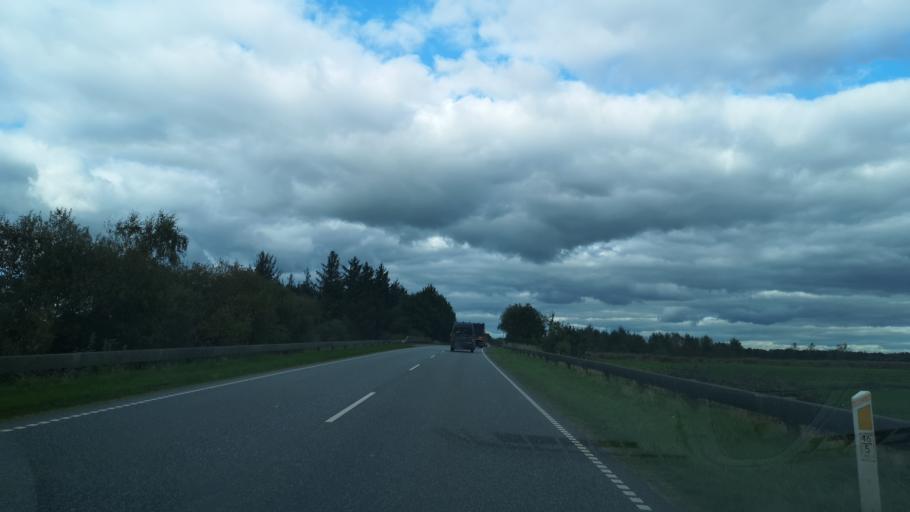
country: DK
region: South Denmark
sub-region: Tonder Kommune
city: Tonder
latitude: 54.9415
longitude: 8.8884
